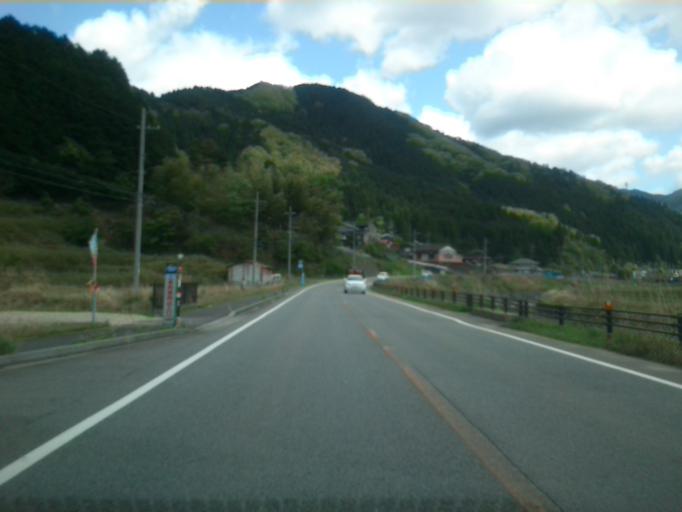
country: JP
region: Kyoto
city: Fukuchiyama
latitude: 35.4290
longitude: 135.0036
